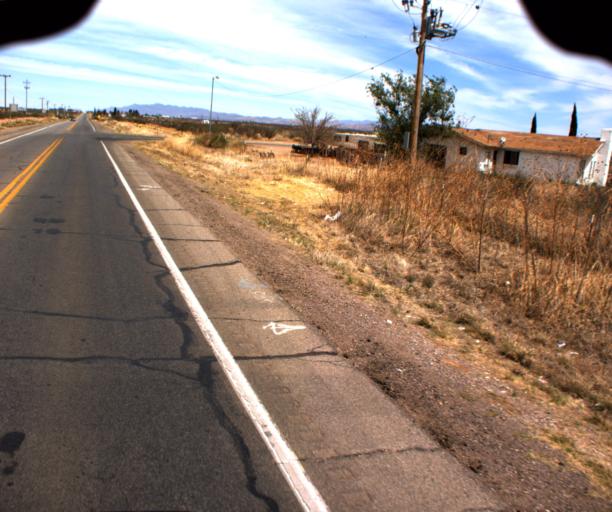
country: US
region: Arizona
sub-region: Cochise County
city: Pirtleville
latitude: 31.3579
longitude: -109.5794
